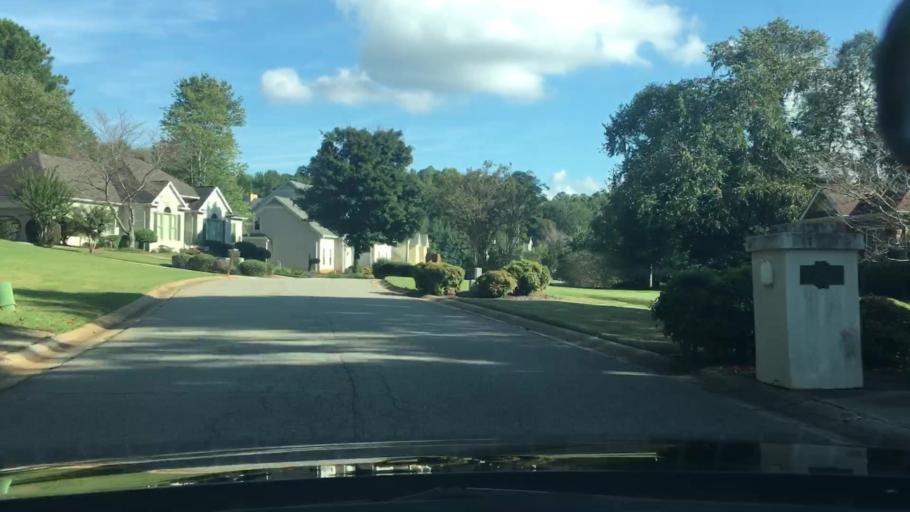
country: US
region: Georgia
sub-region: Coweta County
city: East Newnan
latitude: 33.3985
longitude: -84.7158
